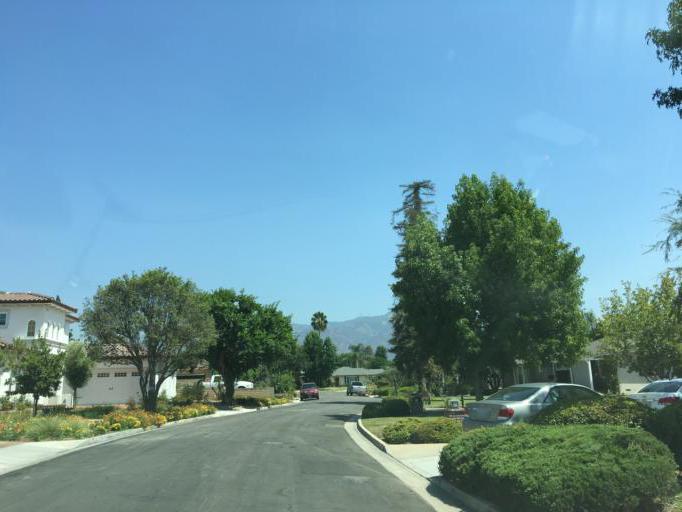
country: US
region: California
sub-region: Los Angeles County
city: San Marino
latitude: 34.1140
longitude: -118.0864
